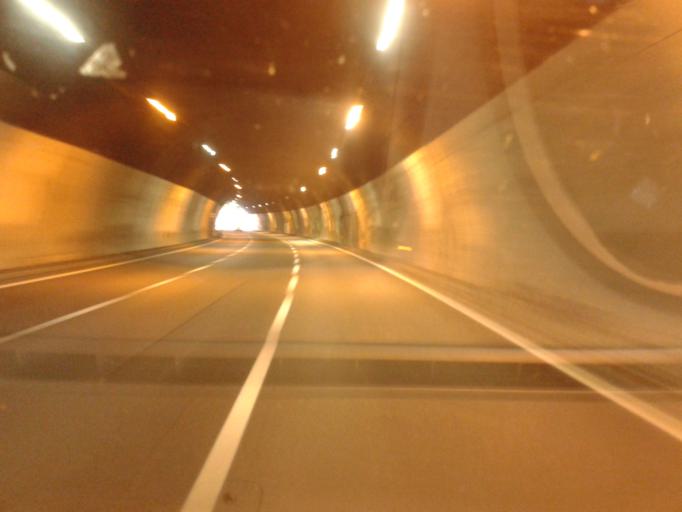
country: IT
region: Liguria
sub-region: Provincia di Genova
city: Rossiglione
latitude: 44.5810
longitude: 8.6610
